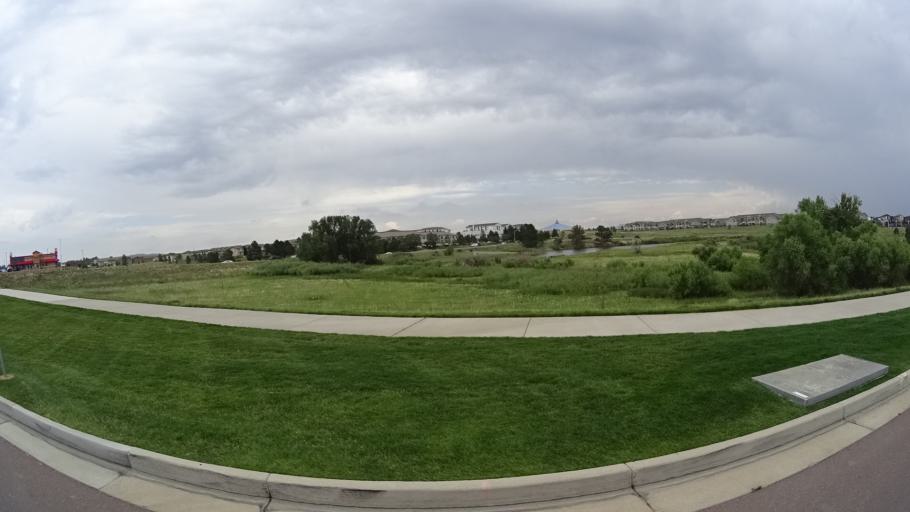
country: US
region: Colorado
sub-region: El Paso County
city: Gleneagle
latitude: 39.0004
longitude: -104.7994
